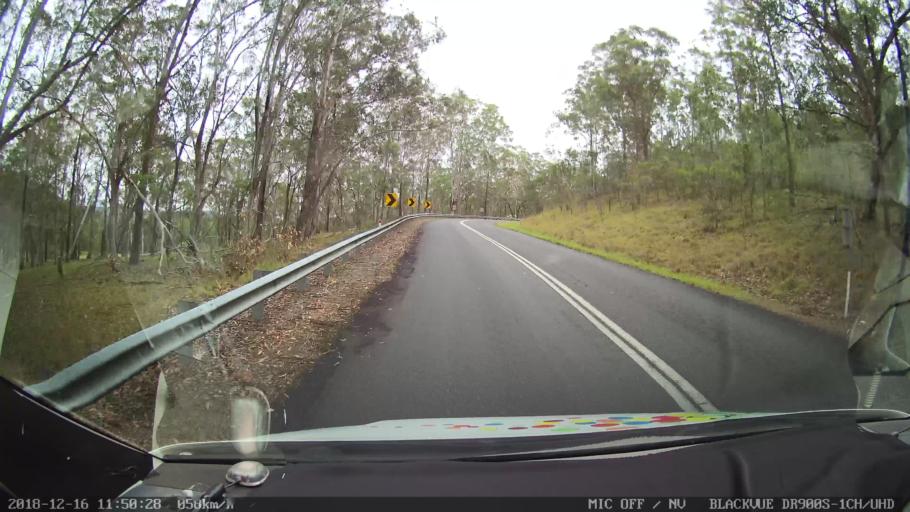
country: AU
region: New South Wales
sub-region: Tenterfield Municipality
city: Carrolls Creek
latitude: -28.9076
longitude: 152.2608
